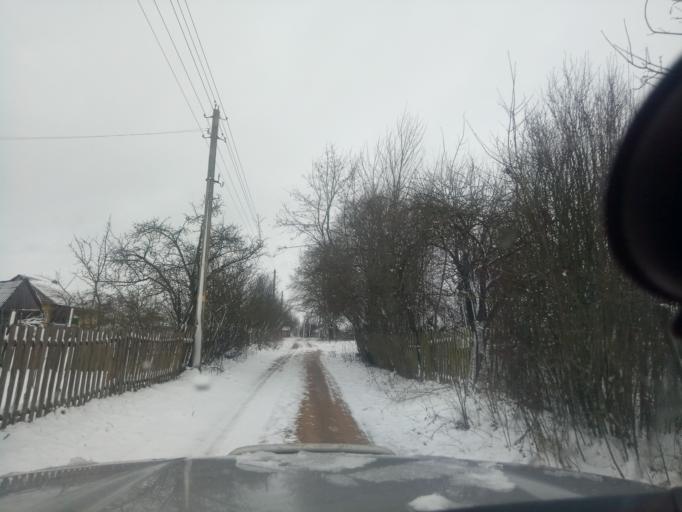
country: BY
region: Minsk
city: Klyetsk
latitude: 53.0239
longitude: 26.7142
